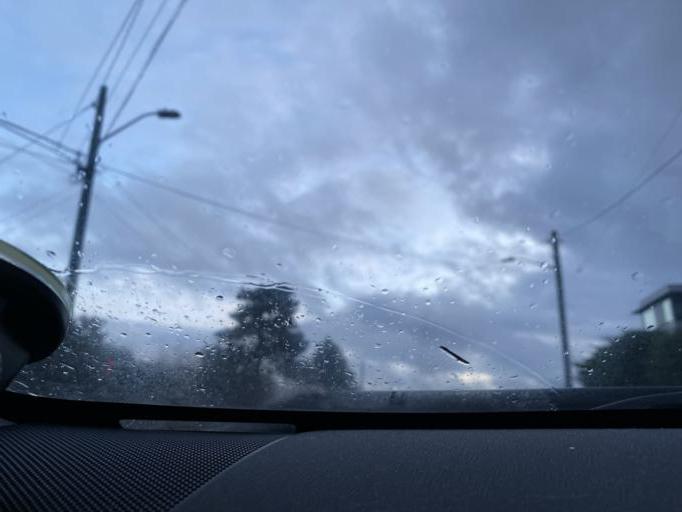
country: US
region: Washington
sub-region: King County
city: Seattle
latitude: 47.6431
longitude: -122.3903
